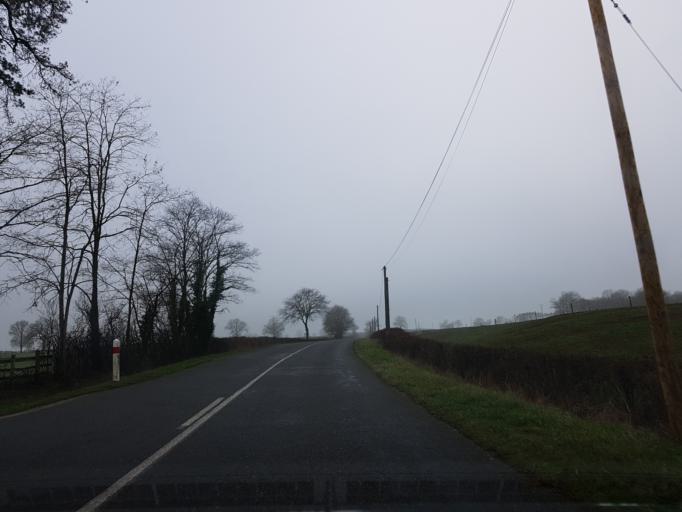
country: FR
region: Bourgogne
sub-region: Departement de Saone-et-Loire
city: Saint-Berain-sous-Sanvignes
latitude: 46.7336
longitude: 4.3405
